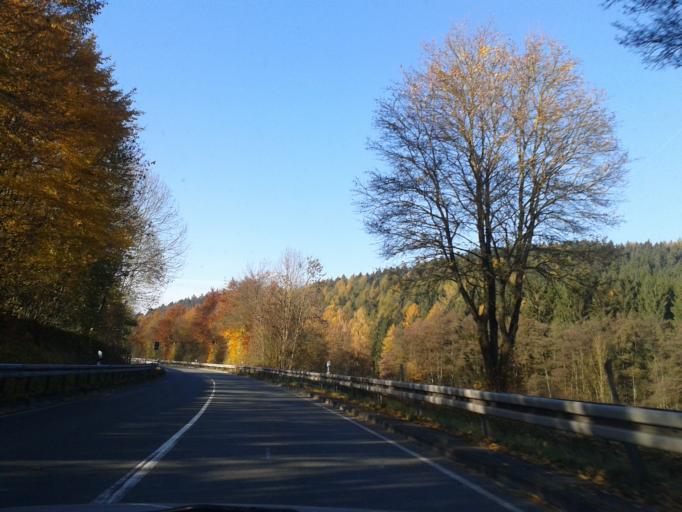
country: DE
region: North Rhine-Westphalia
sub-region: Regierungsbezirk Arnsberg
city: Ruthen
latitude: 51.4351
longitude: 8.4485
